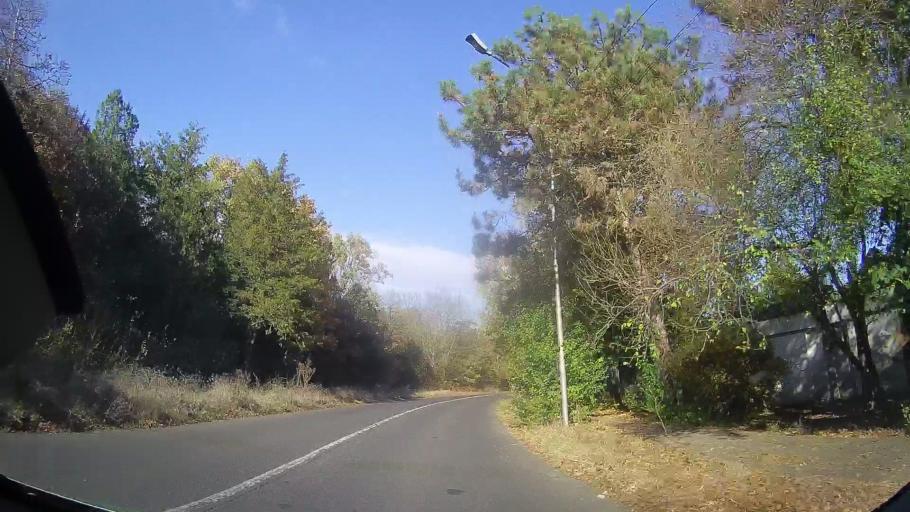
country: RO
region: Constanta
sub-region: Comuna Douazeci si Trei August
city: Douazeci si Trei August
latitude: 43.8701
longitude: 28.5948
